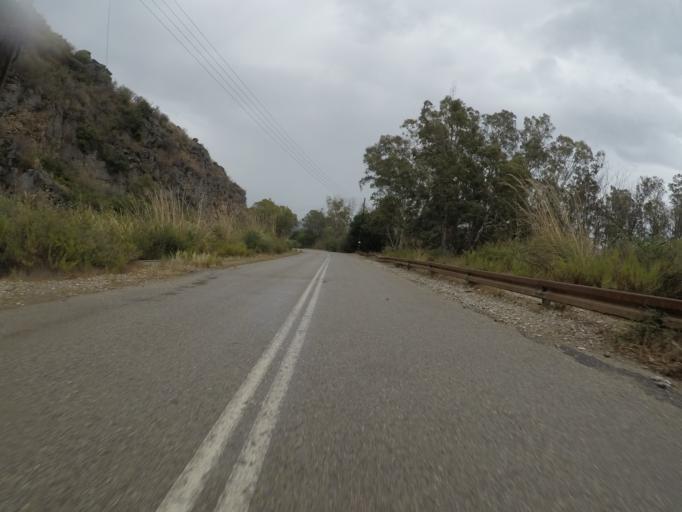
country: GR
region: West Greece
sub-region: Nomos Ileias
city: Zacharo
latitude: 37.5204
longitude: 21.6006
